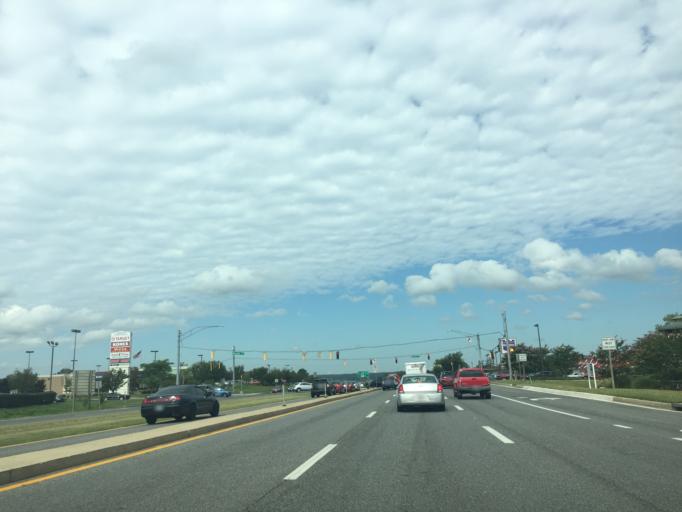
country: US
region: Maryland
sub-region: Anne Arundel County
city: Maryland City
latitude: 39.0976
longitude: -76.8048
